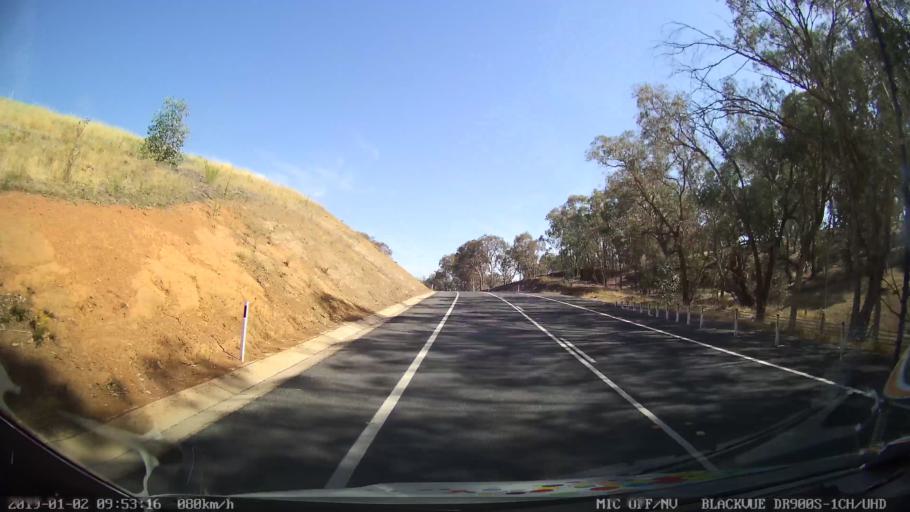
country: AU
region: New South Wales
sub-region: Tumut Shire
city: Tumut
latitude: -35.2499
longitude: 148.2034
